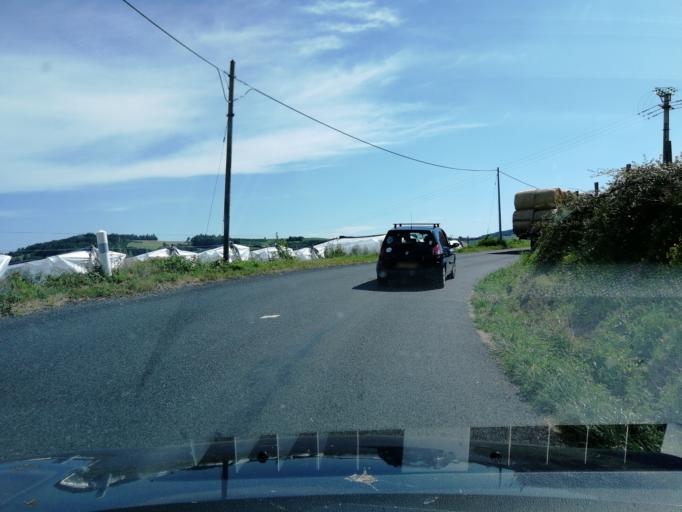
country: FR
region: Rhone-Alpes
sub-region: Departement du Rhone
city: Mornant
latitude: 45.6334
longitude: 4.6339
